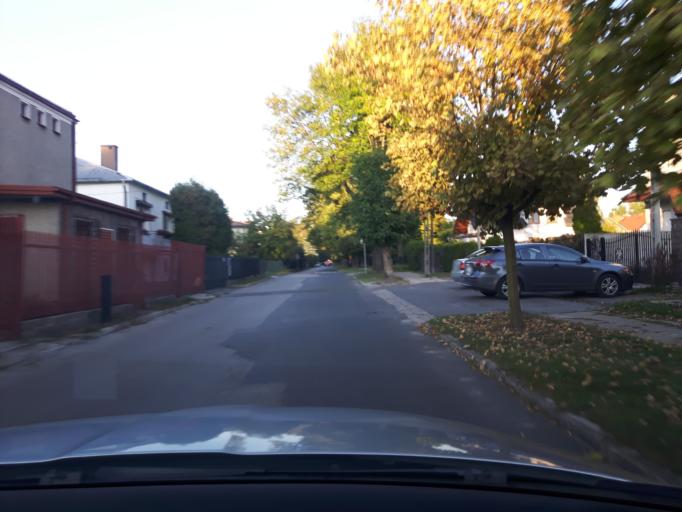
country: PL
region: Masovian Voivodeship
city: Zielonka
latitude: 52.3025
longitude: 21.1532
